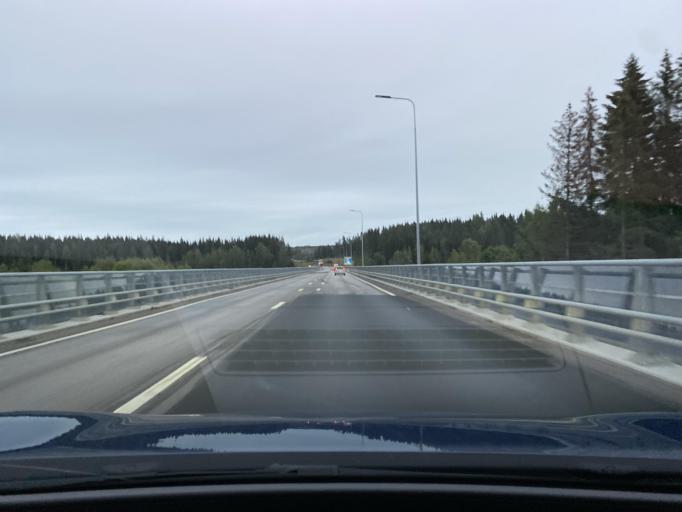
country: FI
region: Paijanne Tavastia
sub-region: Lahti
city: Hollola
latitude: 60.9560
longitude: 25.5625
